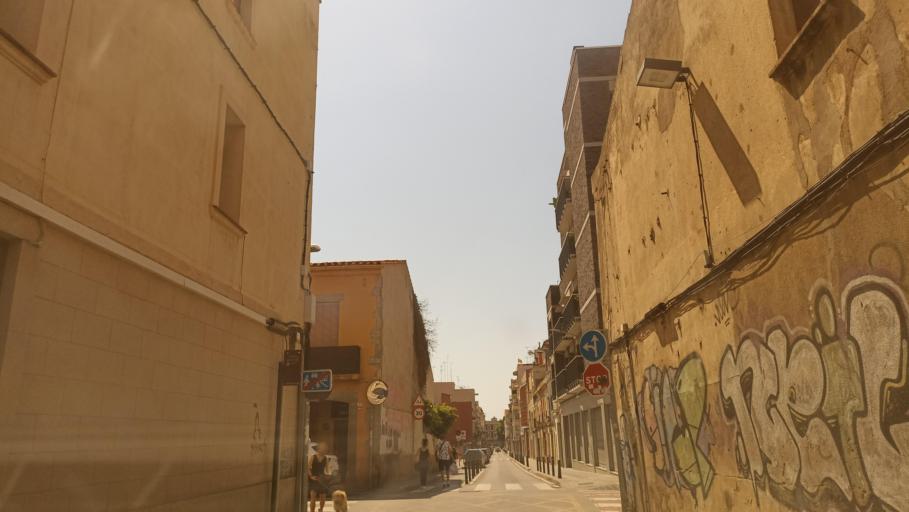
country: ES
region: Catalonia
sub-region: Provincia de Barcelona
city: Mataro
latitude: 41.5359
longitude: 2.4423
